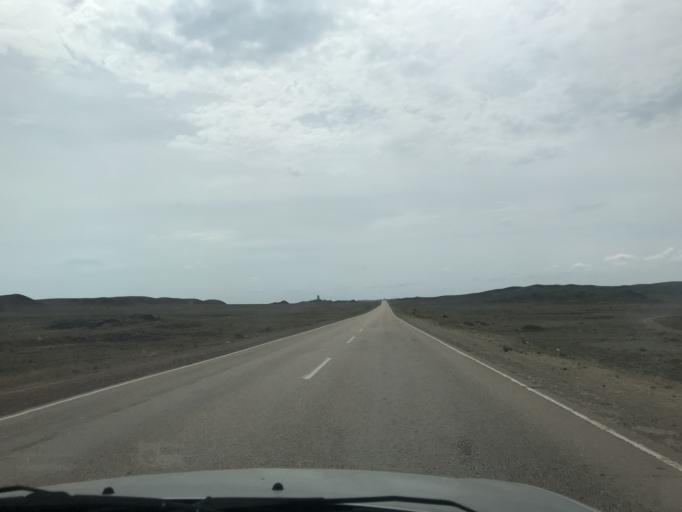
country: KZ
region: Zhambyl
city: Mynaral
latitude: 45.4315
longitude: 73.6166
